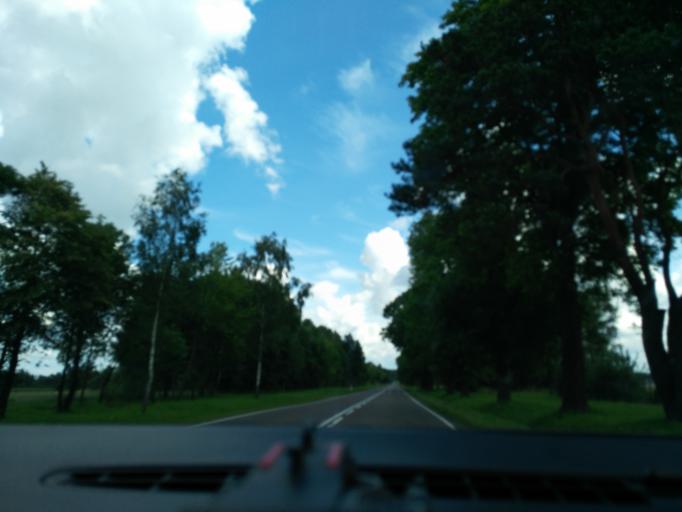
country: PL
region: Podlasie
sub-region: Powiat bielski
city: Bielsk Podlaski
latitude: 52.7279
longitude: 23.1511
